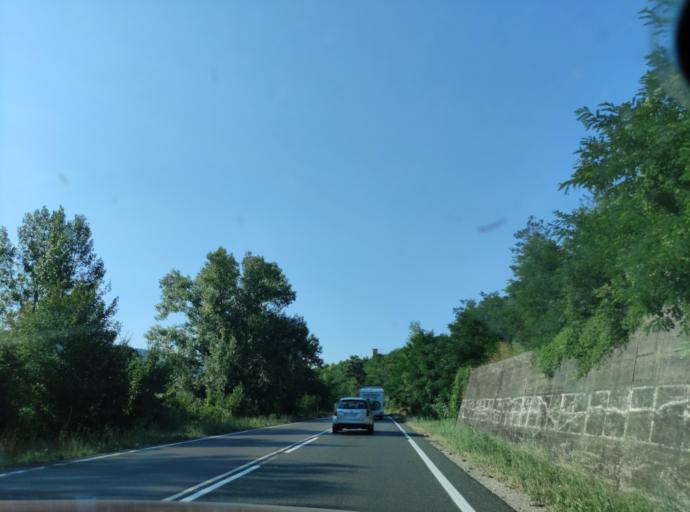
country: BG
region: Blagoevgrad
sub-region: Obshtina Simitli
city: Simitli
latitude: 41.8783
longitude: 23.1207
